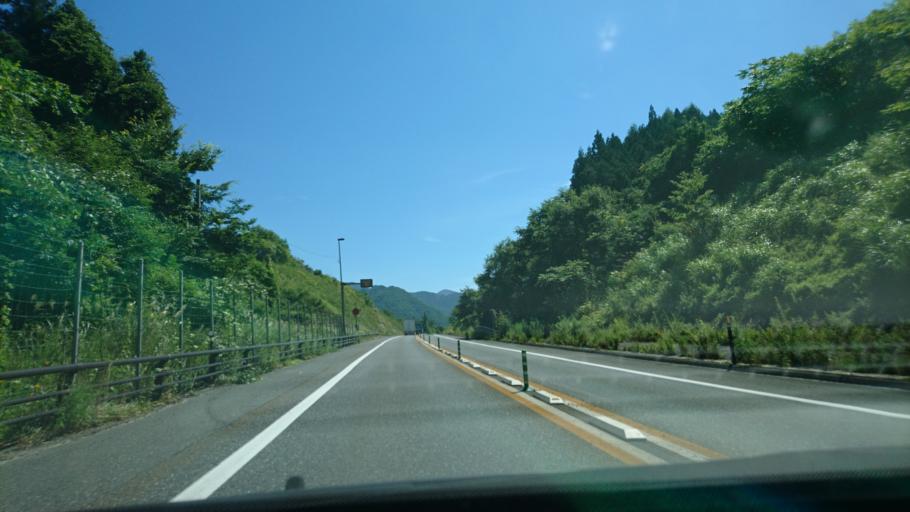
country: JP
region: Iwate
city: Tono
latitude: 39.2631
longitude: 141.6026
